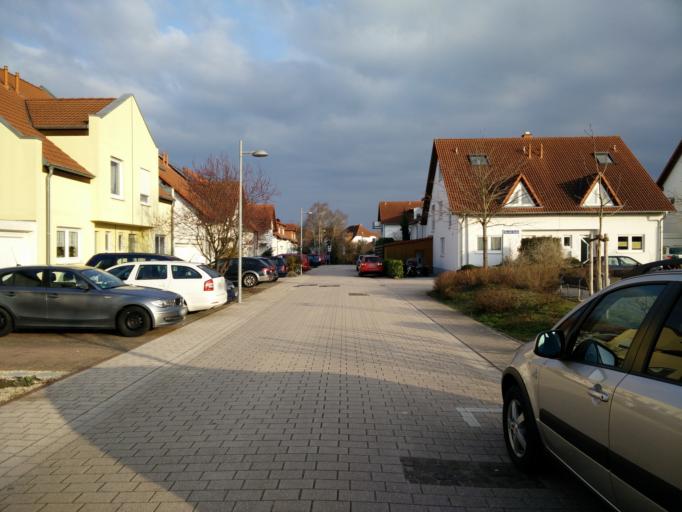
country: DE
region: Rheinland-Pfalz
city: Speyer
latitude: 49.3306
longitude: 8.4340
